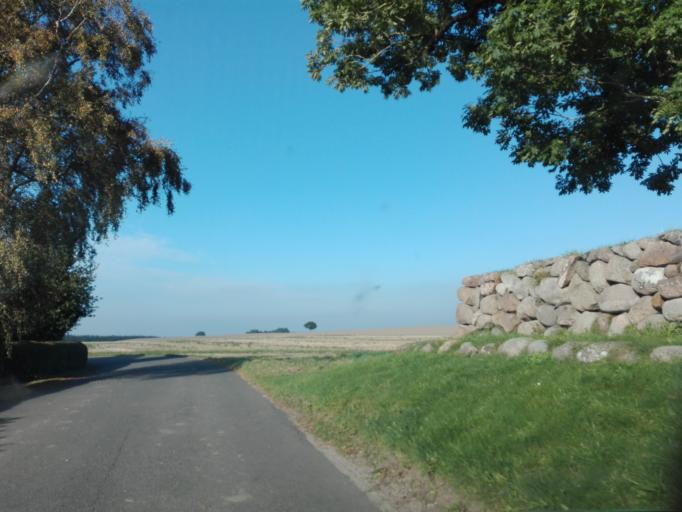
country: DK
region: Central Jutland
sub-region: Odder Kommune
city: Odder
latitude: 55.9301
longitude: 10.1914
